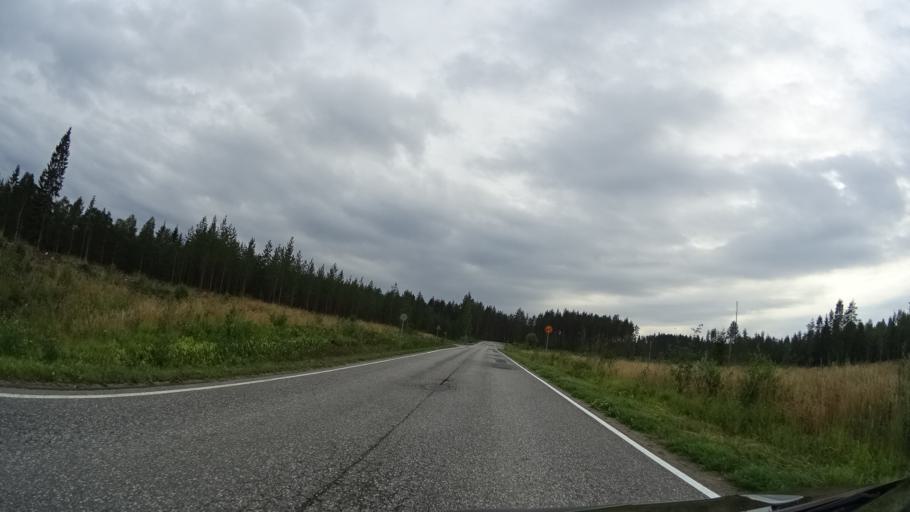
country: FI
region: Southern Savonia
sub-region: Savonlinna
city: Punkaharju
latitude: 61.7546
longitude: 29.4501
